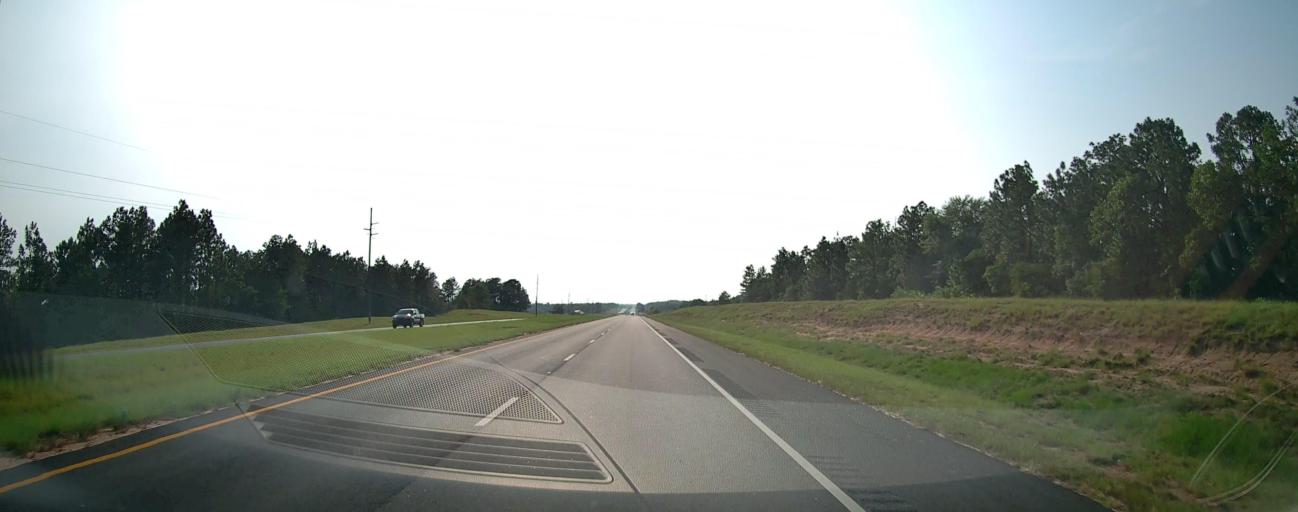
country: US
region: Georgia
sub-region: Taylor County
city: Butler
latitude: 32.5815
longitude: -84.3261
